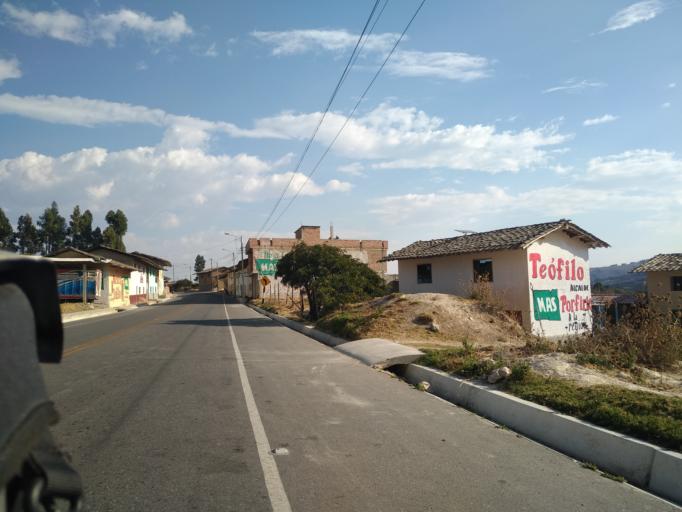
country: PE
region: Cajamarca
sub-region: San Marcos
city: San Marcos
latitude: -7.3834
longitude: -78.1255
